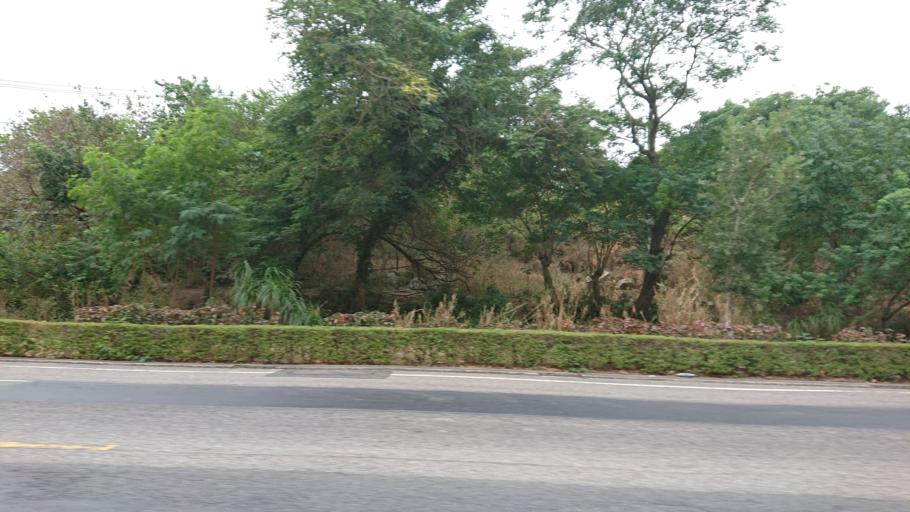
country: TW
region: Fukien
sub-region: Kinmen
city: Jincheng
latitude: 24.4411
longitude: 118.3912
